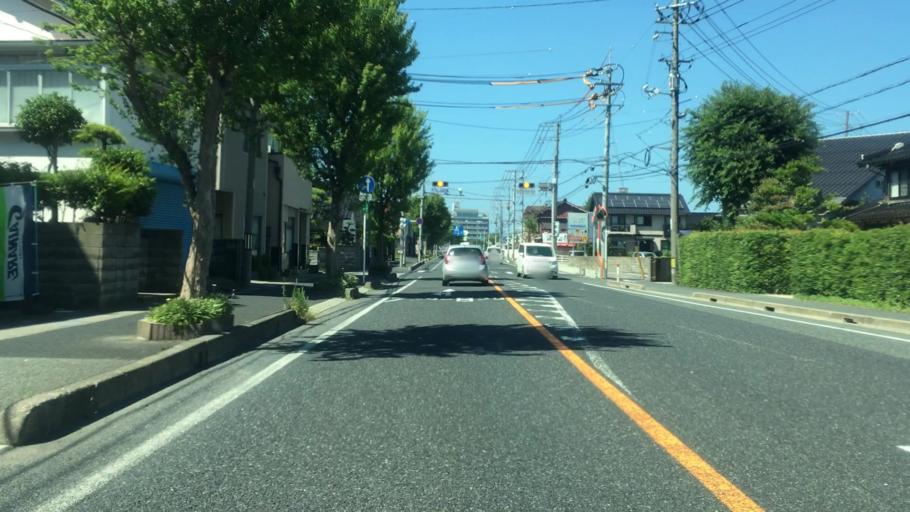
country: JP
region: Tottori
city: Tottori
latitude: 35.4868
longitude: 134.2210
